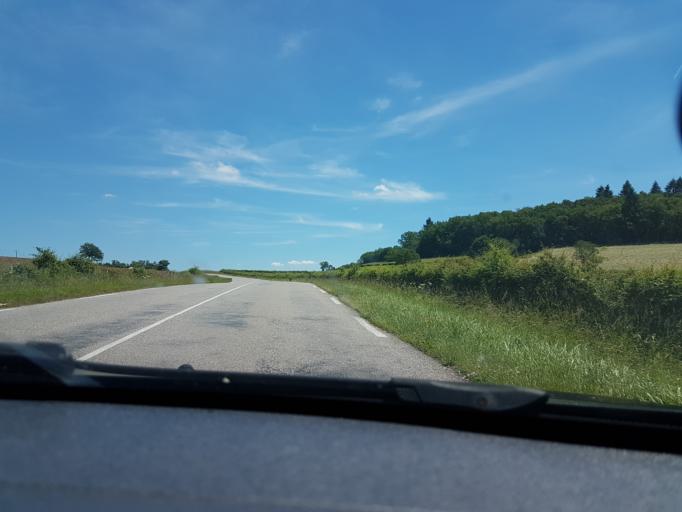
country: FR
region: Bourgogne
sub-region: Departement de Saone-et-Loire
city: Epinac
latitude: 46.9721
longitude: 4.5140
